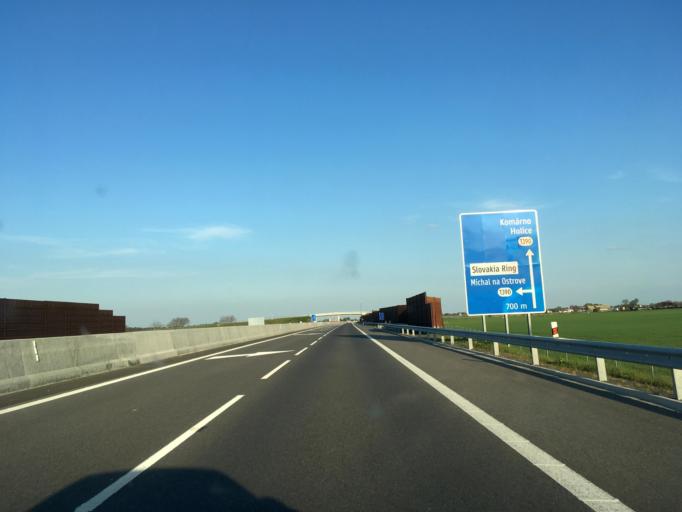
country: SK
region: Trnavsky
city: Dunajska Streda
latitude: 48.0057
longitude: 17.4810
